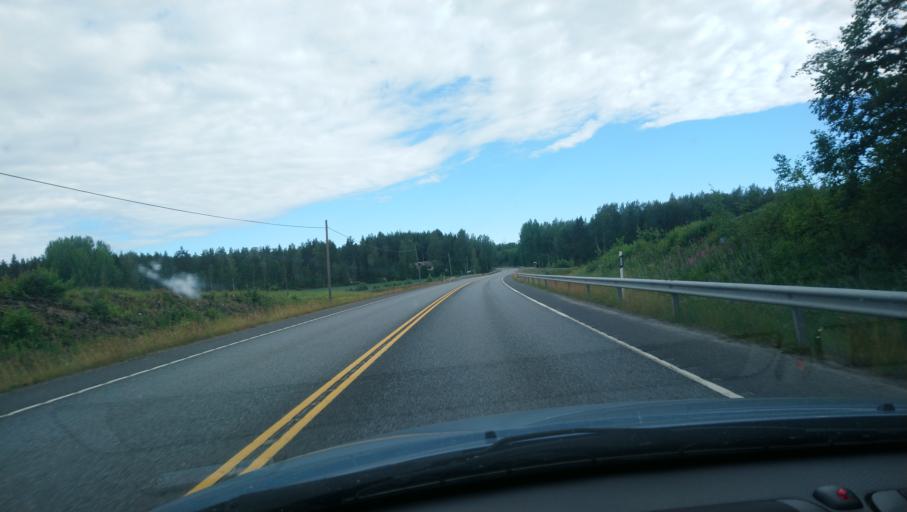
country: FI
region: Uusimaa
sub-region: Porvoo
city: Porvoo
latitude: 60.4206
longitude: 25.5790
